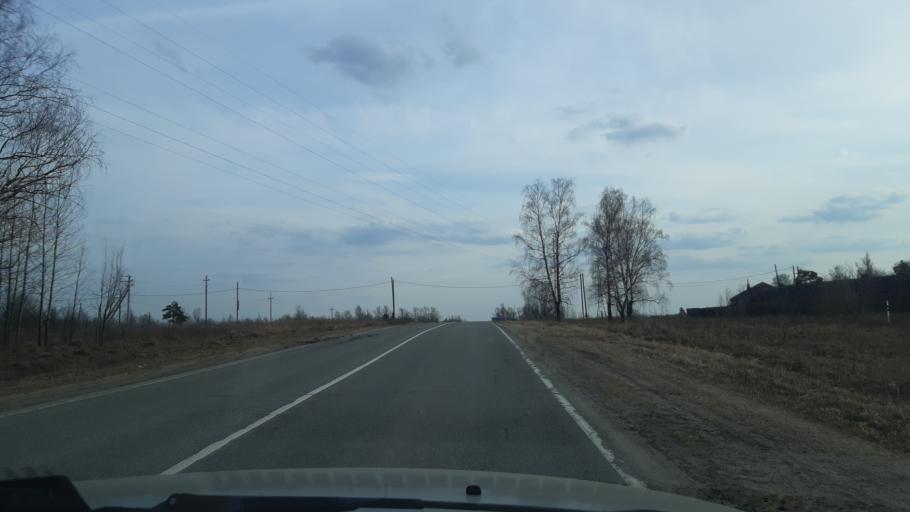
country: RU
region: Vladimir
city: Luknovo
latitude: 56.2011
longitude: 42.0334
